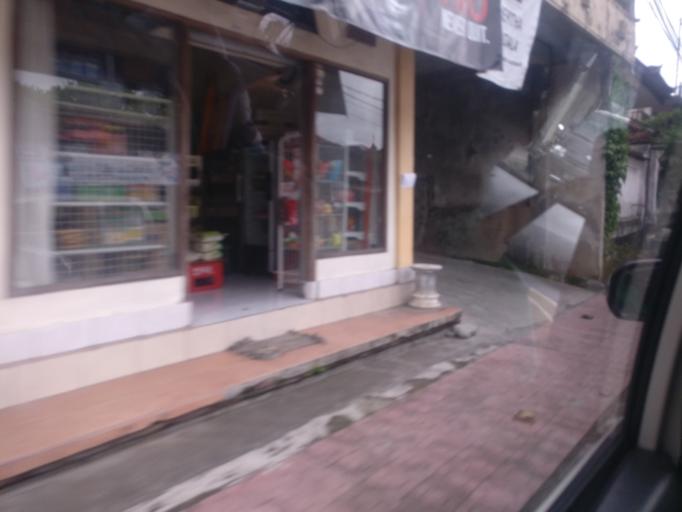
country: ID
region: Bali
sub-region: Kabupaten Gianyar
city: Ubud
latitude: -8.5170
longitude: 115.2668
